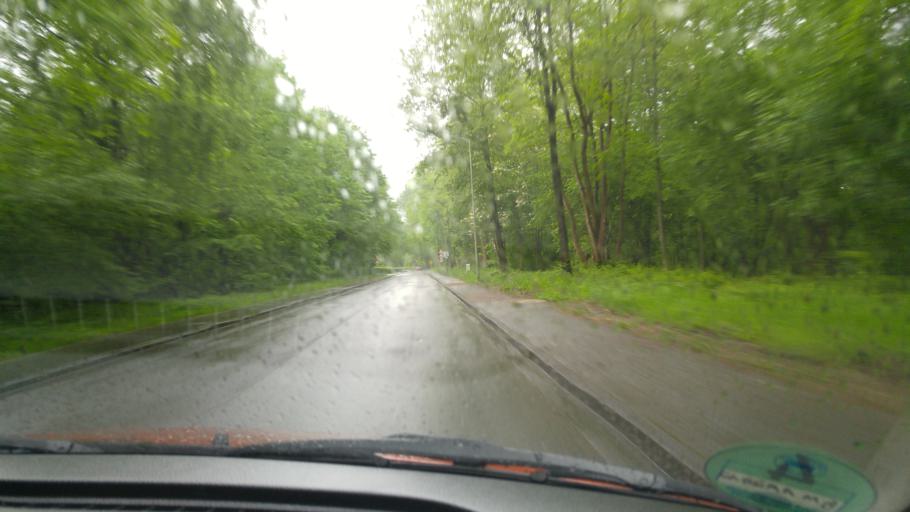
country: DE
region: North Rhine-Westphalia
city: Waldbrol
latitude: 50.8736
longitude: 7.6260
